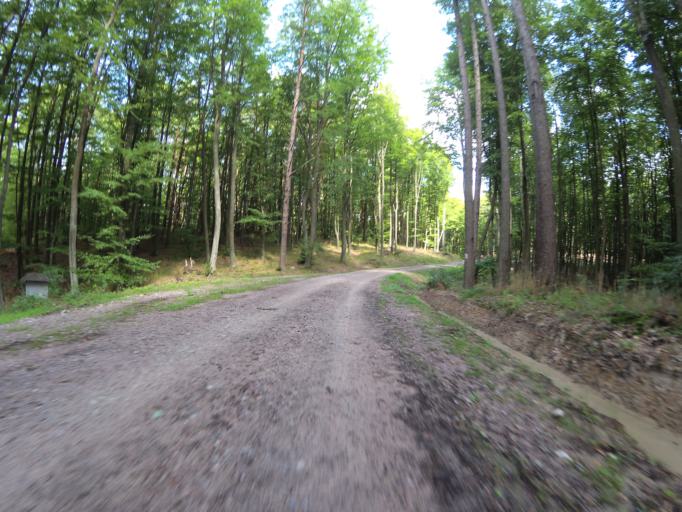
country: PL
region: Pomeranian Voivodeship
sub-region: Powiat wejherowski
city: Bojano
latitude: 54.5172
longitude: 18.4250
